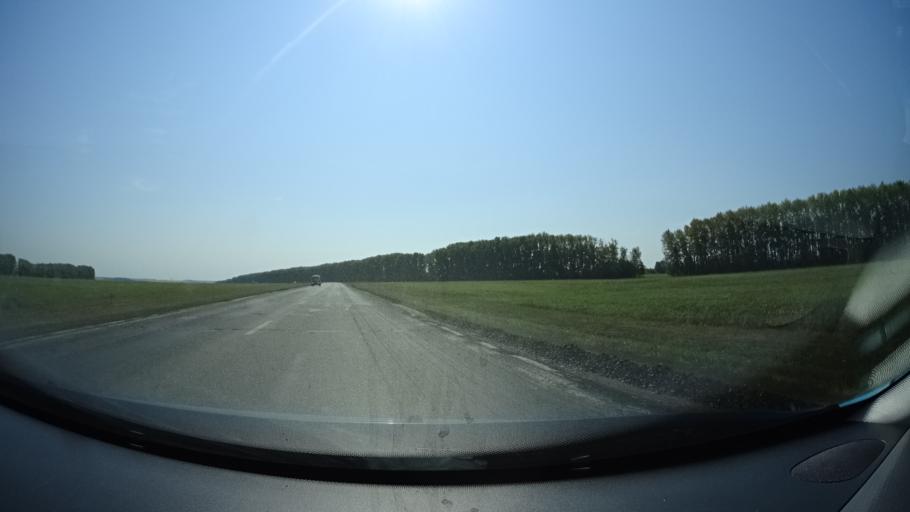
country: RU
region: Bashkortostan
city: Kabakovo
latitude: 54.4539
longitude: 55.9715
